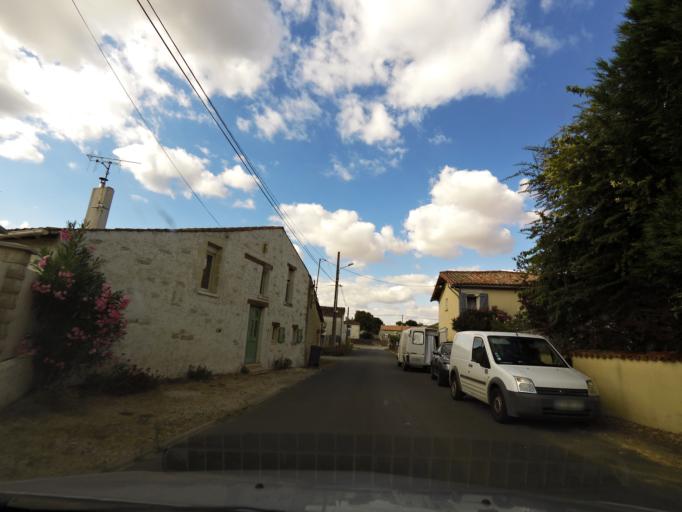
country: FR
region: Poitou-Charentes
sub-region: Departement des Deux-Sevres
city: Beauvoir-sur-Niort
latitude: 46.1469
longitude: -0.3941
